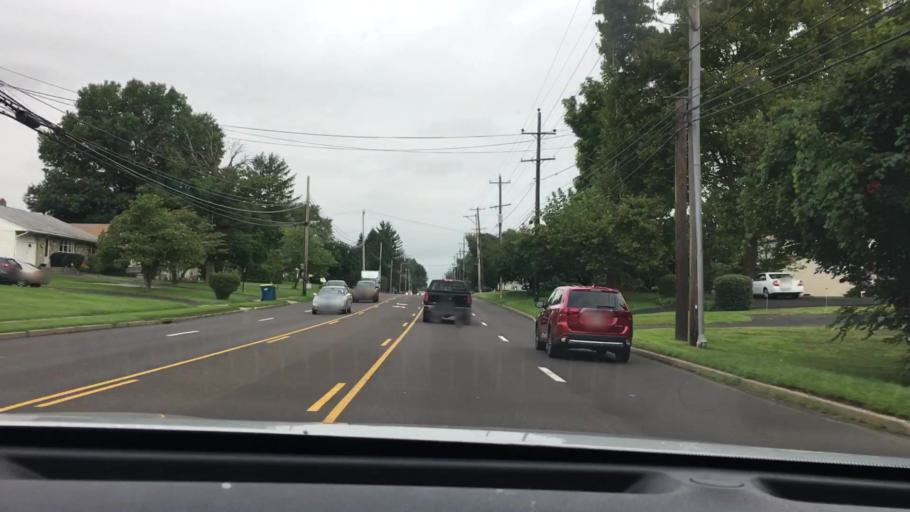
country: US
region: Pennsylvania
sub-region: Montgomery County
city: Hatboro
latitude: 40.1951
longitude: -75.1117
